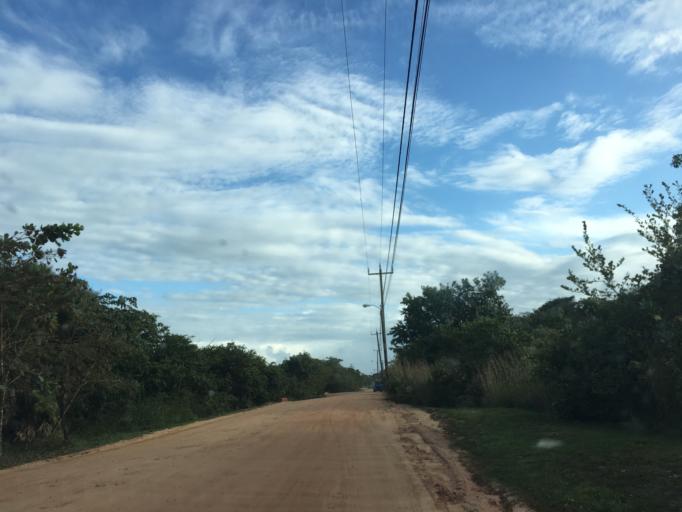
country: BZ
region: Stann Creek
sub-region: Dangriga
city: Dangriga
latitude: 16.8435
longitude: -88.2761
